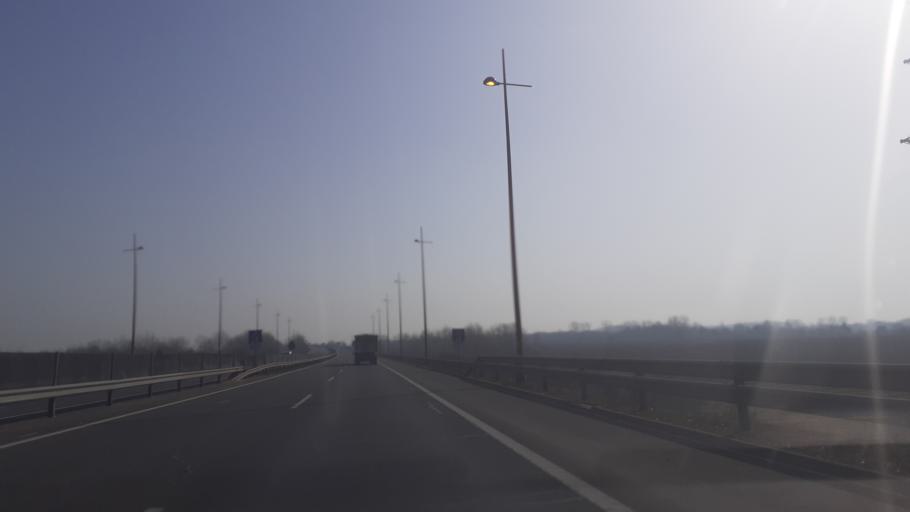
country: HU
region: Bacs-Kiskun
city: Dunavecse
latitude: 46.9008
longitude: 18.9657
